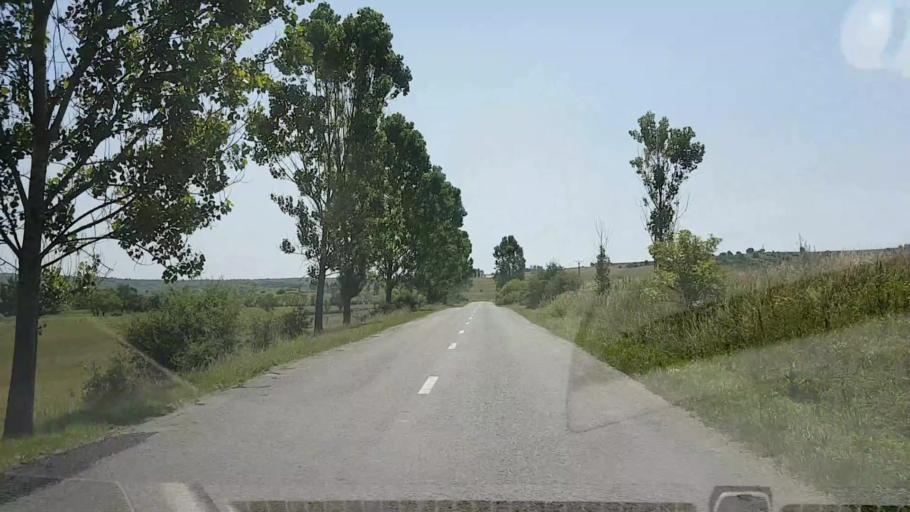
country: RO
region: Sibiu
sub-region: Comuna Merghindeal
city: Merghindeal
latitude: 45.9603
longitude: 24.7554
